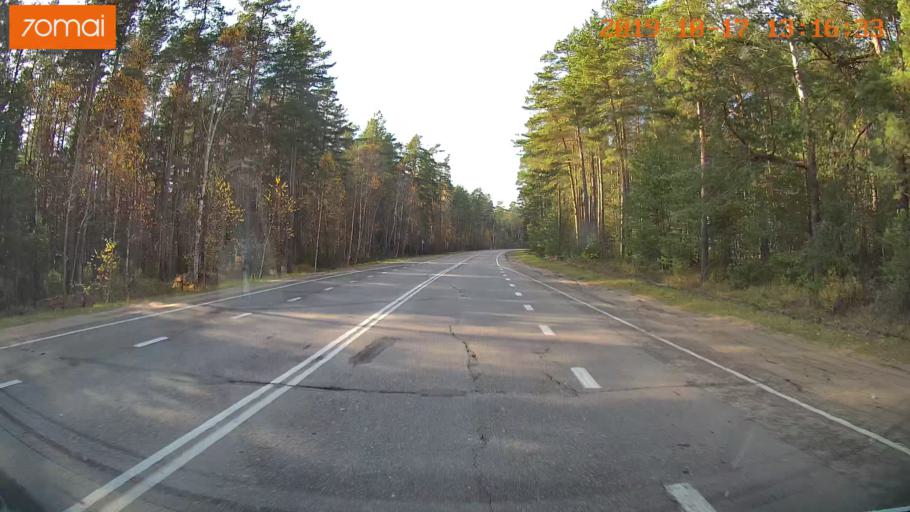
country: RU
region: Rjazan
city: Gus'-Zheleznyy
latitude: 55.0492
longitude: 41.1379
